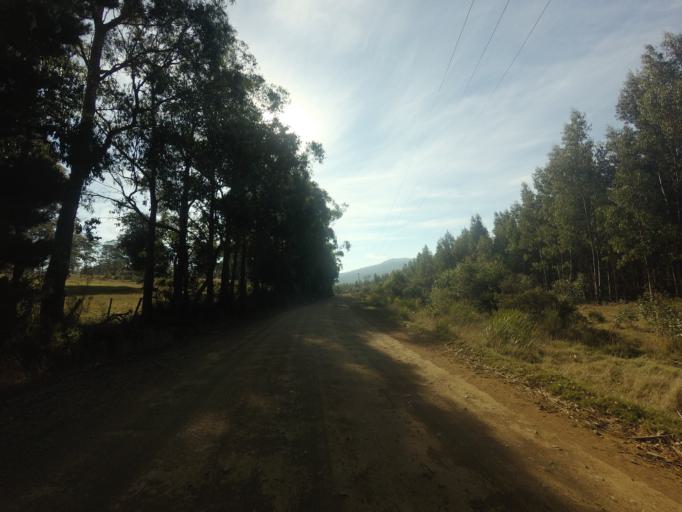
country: AU
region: Tasmania
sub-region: Sorell
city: Sorell
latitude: -42.4967
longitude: 147.5284
